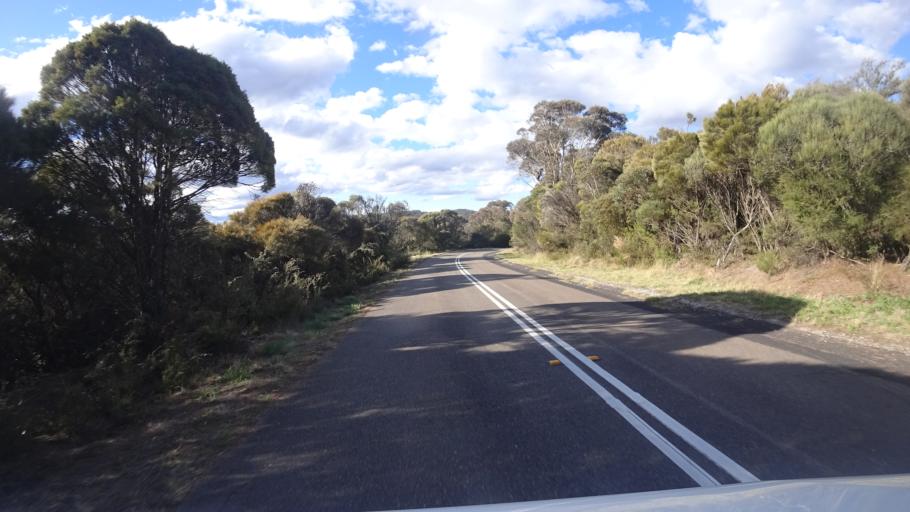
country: AU
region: New South Wales
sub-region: Blue Mountains Municipality
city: Katoomba
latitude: -33.7192
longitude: 150.2867
